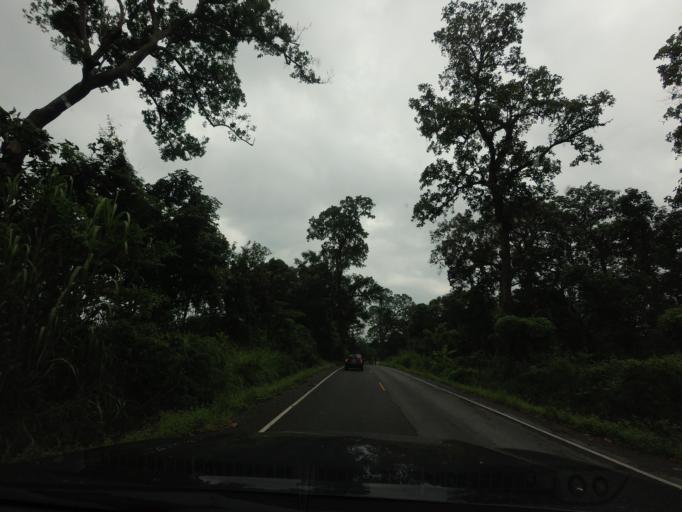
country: TH
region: Nong Khai
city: Sangkhom
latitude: 18.0387
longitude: 102.3248
